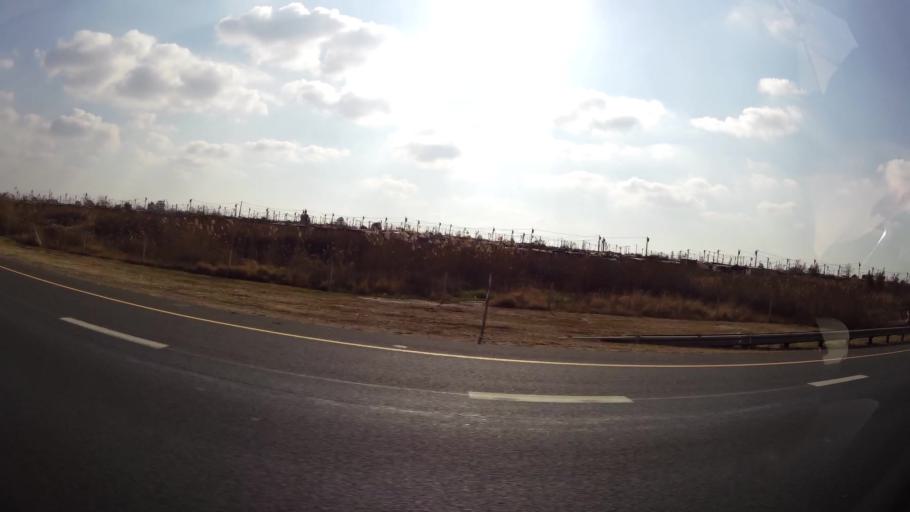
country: ZA
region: Gauteng
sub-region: Ekurhuleni Metropolitan Municipality
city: Benoni
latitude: -26.1664
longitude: 28.3745
